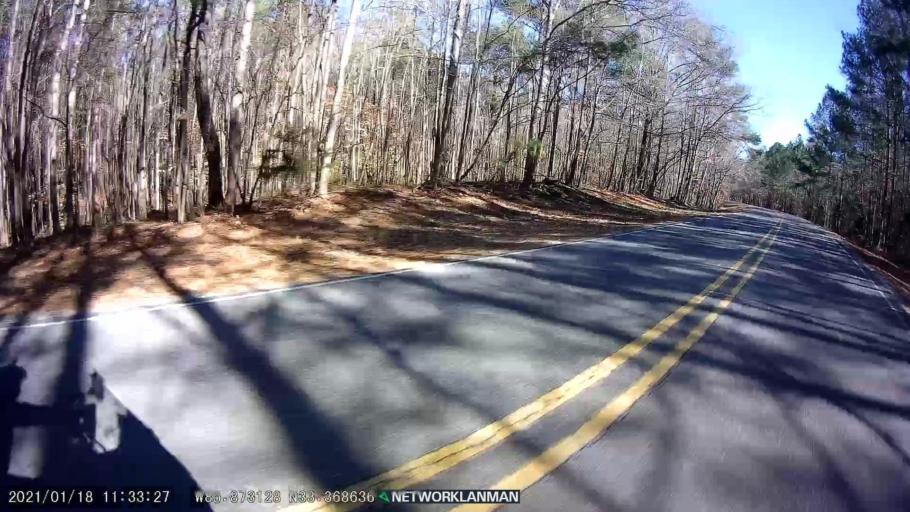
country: US
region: Alabama
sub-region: Clay County
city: Ashland
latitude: 33.3685
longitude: -85.8726
